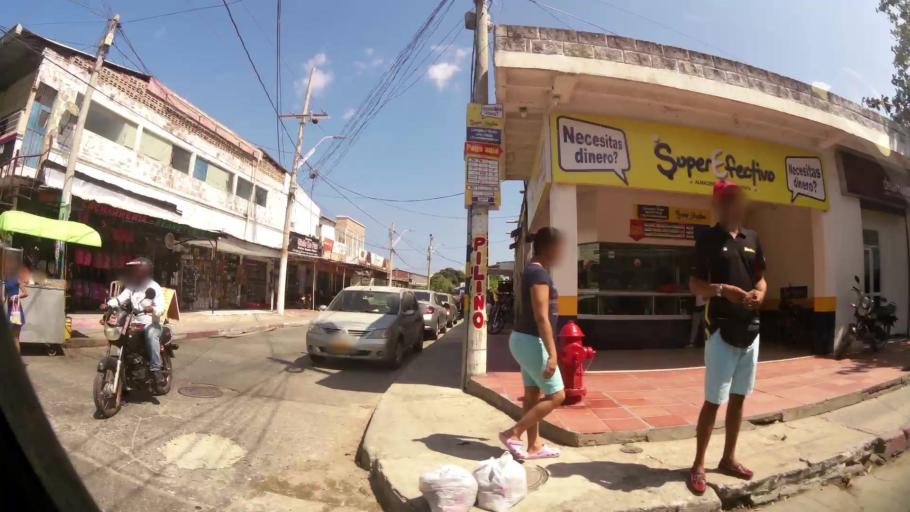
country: CO
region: Atlantico
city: Barranquilla
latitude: 10.9659
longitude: -74.8340
